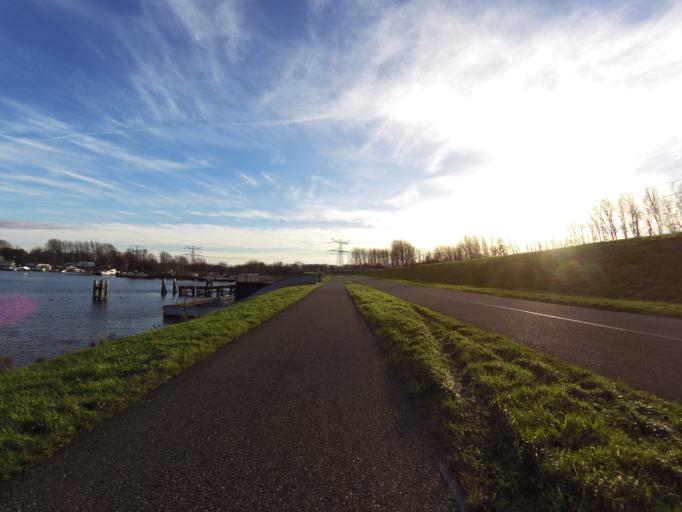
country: NL
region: South Holland
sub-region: Gemeente Rotterdam
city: Hoek van Holland
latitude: 51.9263
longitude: 4.1031
